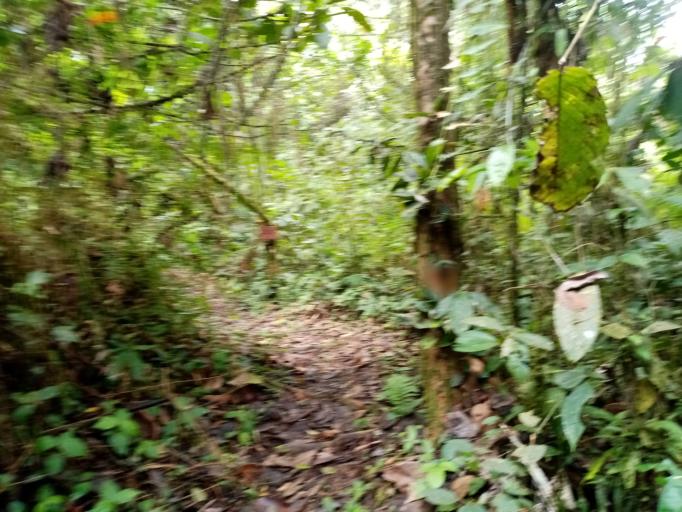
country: EC
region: Napo
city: Tena
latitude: -0.9699
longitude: -77.7977
